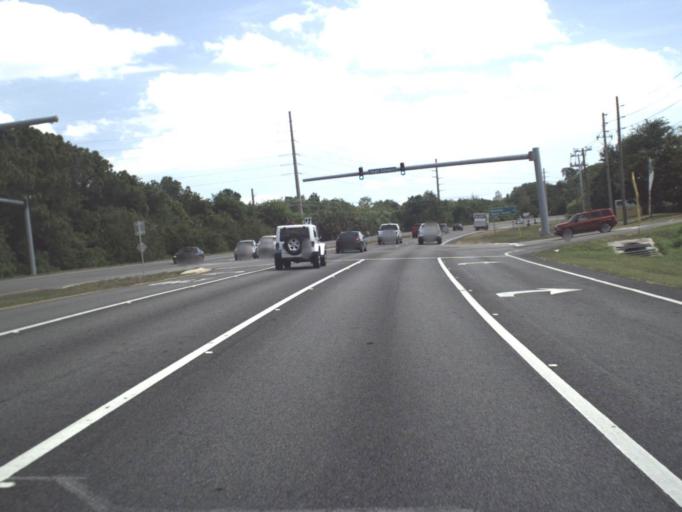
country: US
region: Florida
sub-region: Brevard County
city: Titusville
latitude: 28.5533
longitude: -80.8410
